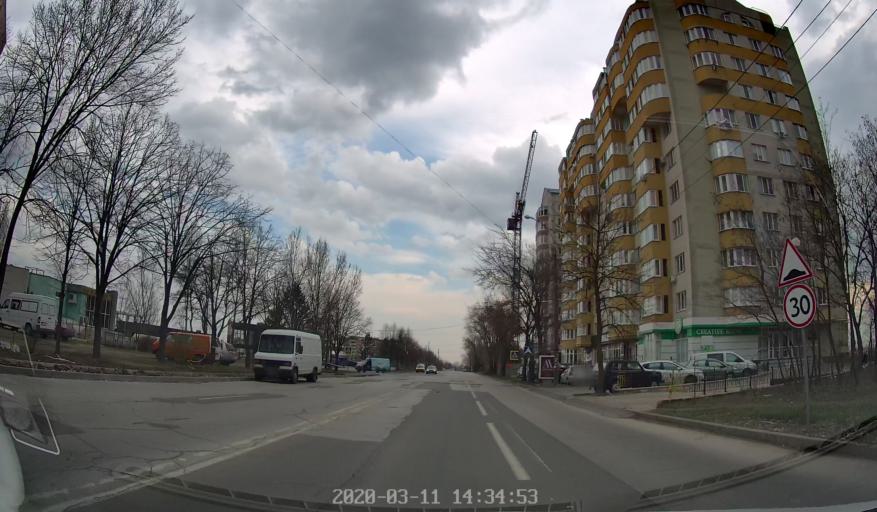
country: MD
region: Chisinau
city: Chisinau
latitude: 47.0331
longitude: 28.8783
